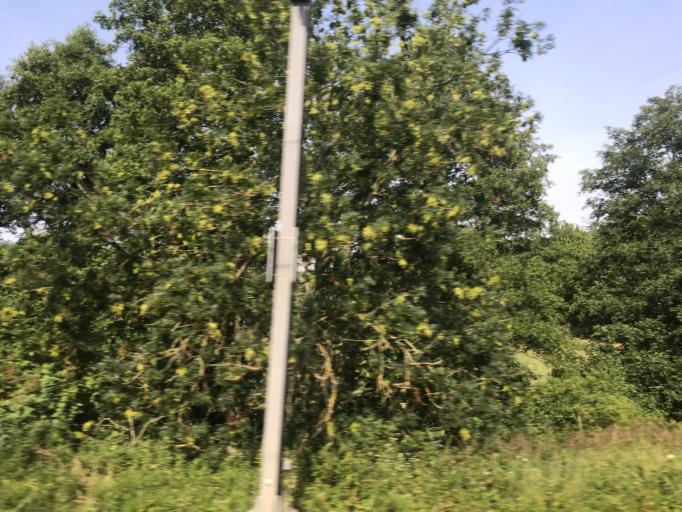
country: CZ
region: Central Bohemia
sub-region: Okres Benesov
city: Benesov
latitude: 49.7990
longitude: 14.7021
